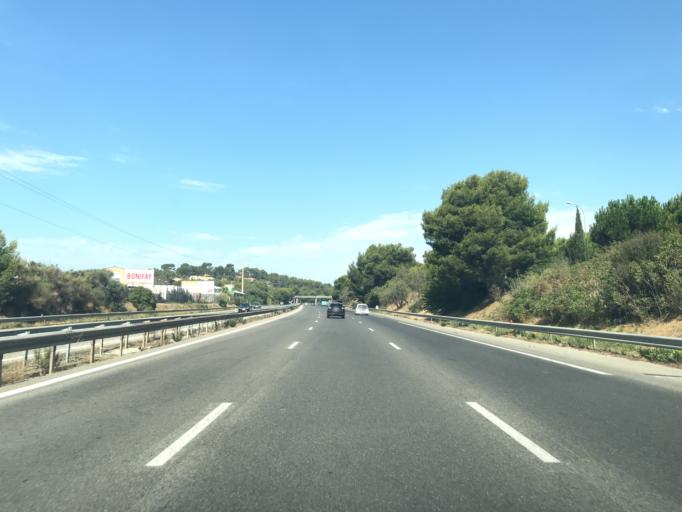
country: FR
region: Provence-Alpes-Cote d'Azur
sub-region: Departement du Var
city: Sanary-sur-Mer
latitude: 43.1269
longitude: 5.8233
